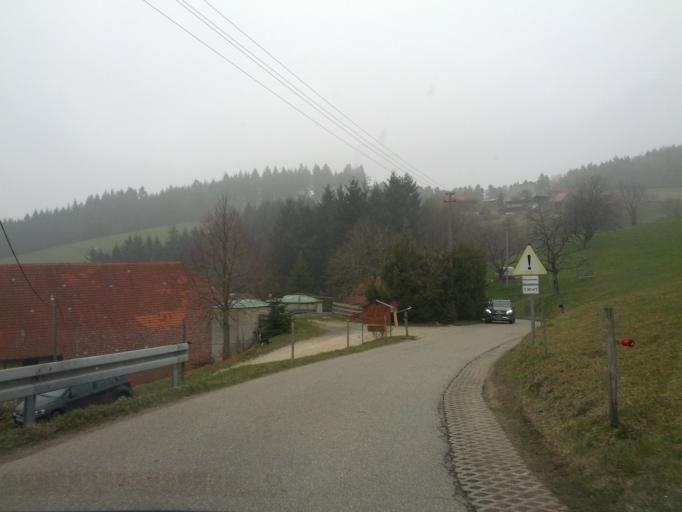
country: DE
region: Baden-Wuerttemberg
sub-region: Freiburg Region
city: Au
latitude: 47.9417
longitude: 7.8461
